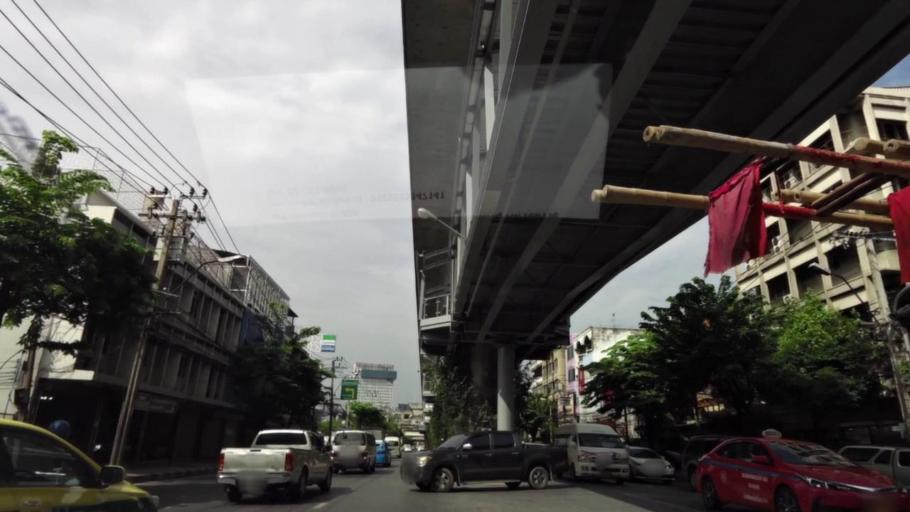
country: TH
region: Bangkok
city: Phra Khanong
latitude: 13.6772
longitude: 100.6084
